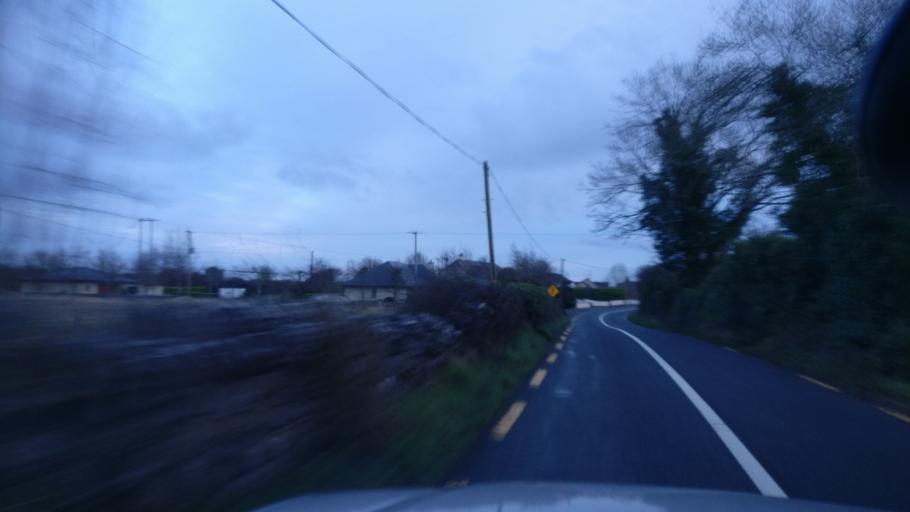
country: IE
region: Connaught
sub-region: County Galway
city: Athenry
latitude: 53.2510
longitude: -8.6678
